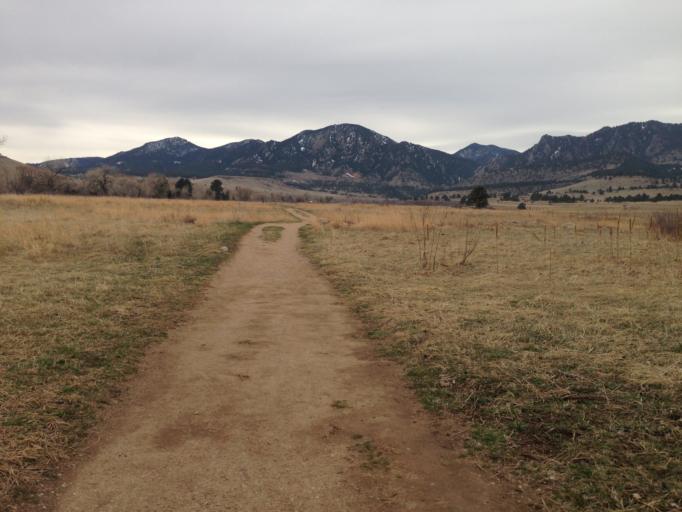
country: US
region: Colorado
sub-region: Boulder County
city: Boulder
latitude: 39.9528
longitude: -105.2429
